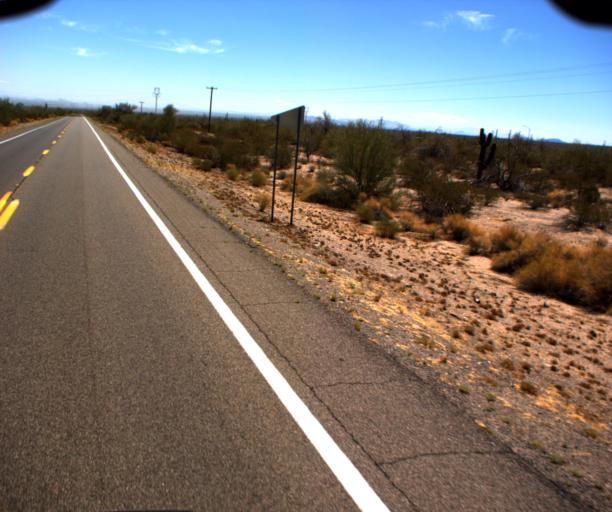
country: US
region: Arizona
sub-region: Pinal County
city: Maricopa
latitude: 32.8398
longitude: -112.1162
